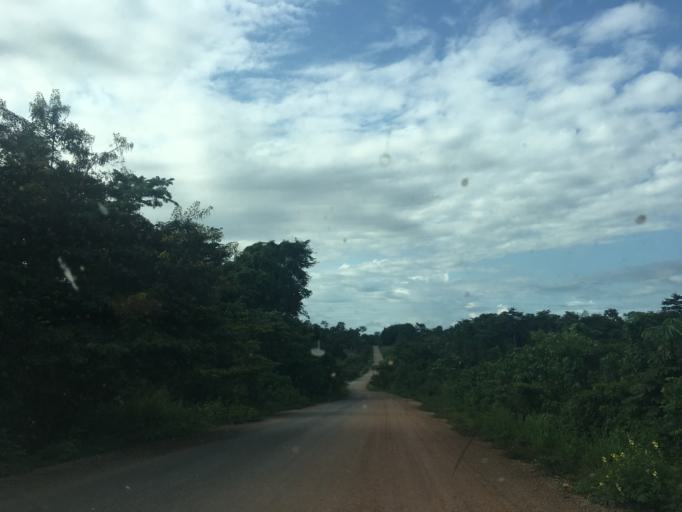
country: GH
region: Western
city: Wassa-Akropong
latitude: 5.9844
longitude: -2.4136
